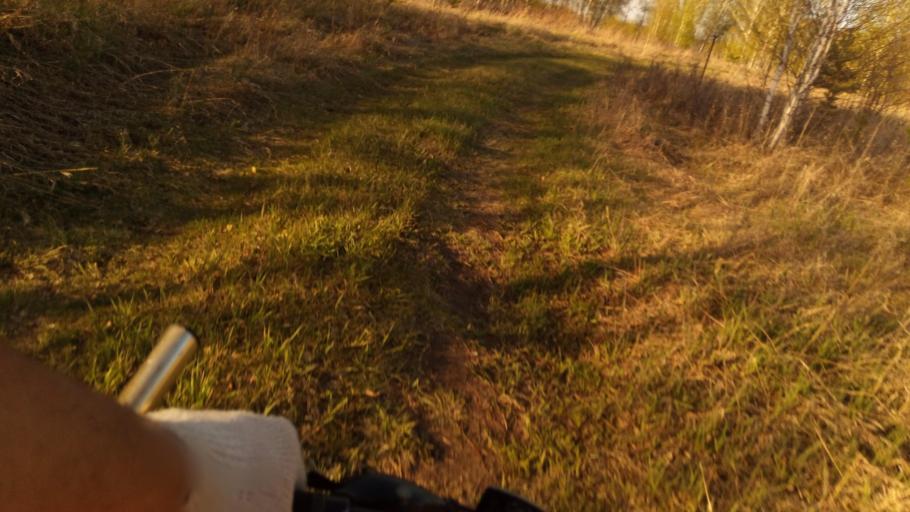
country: RU
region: Chelyabinsk
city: Timiryazevskiy
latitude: 54.9951
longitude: 60.8567
